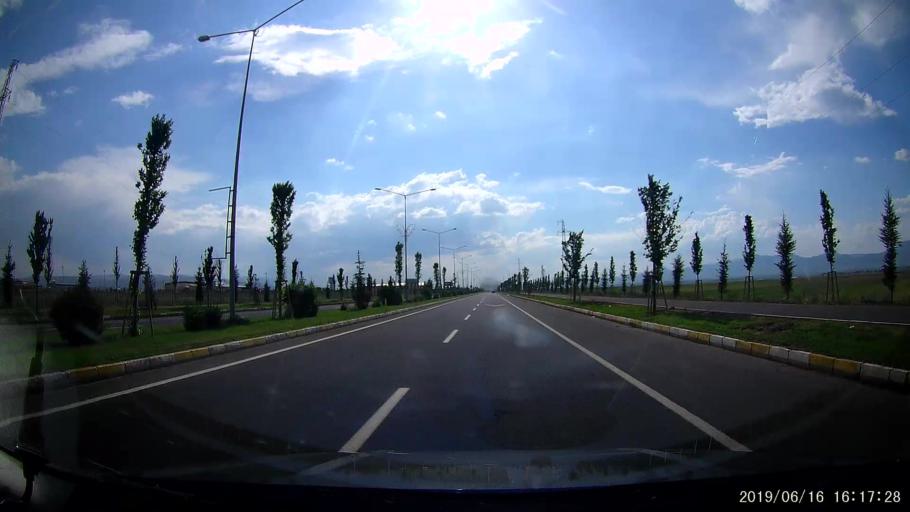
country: TR
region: Erzurum
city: Ilica
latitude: 39.9640
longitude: 41.1861
